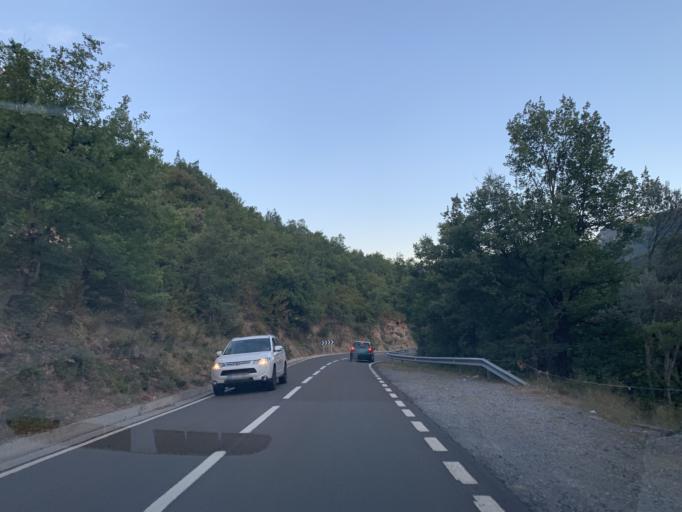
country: ES
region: Aragon
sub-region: Provincia de Huesca
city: Fiscal
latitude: 42.5186
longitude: -0.1286
